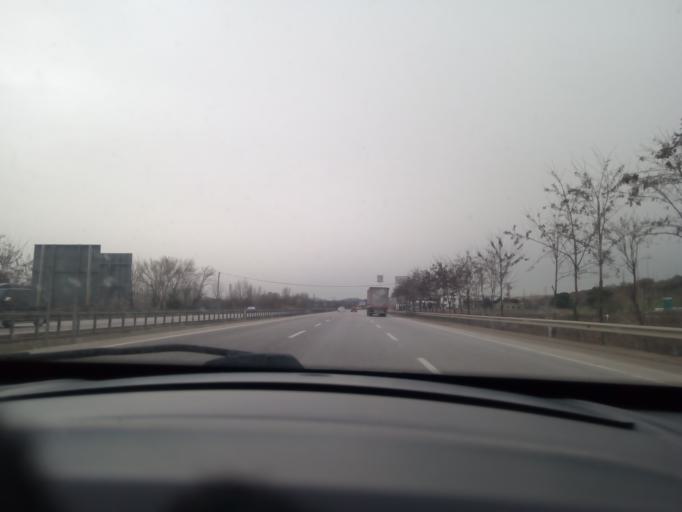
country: TR
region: Balikesir
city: Susurluk
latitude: 39.9683
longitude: 28.1716
